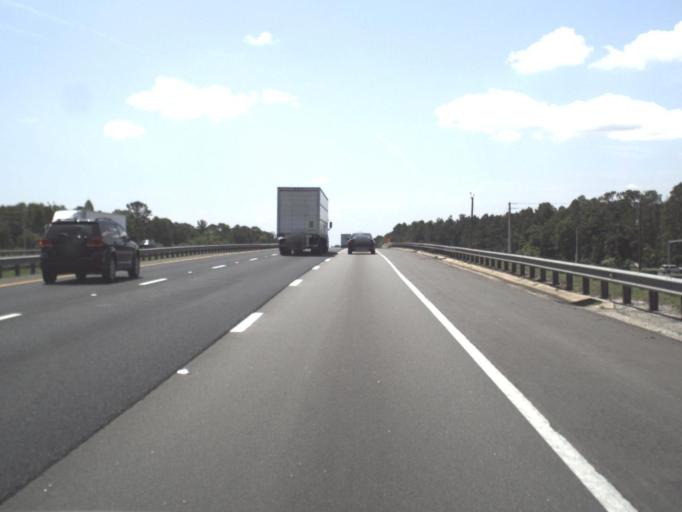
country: US
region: Florida
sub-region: Nassau County
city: Yulee
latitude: 30.6210
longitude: -81.6507
